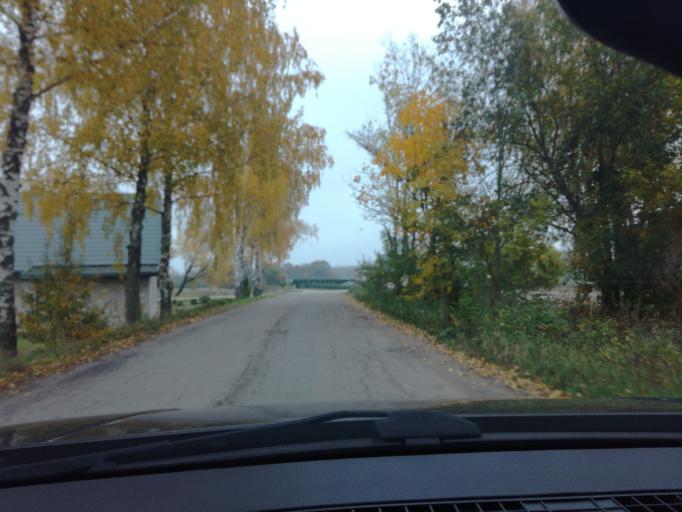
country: LT
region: Alytaus apskritis
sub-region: Alytus
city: Alytus
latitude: 54.4174
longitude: 23.9779
